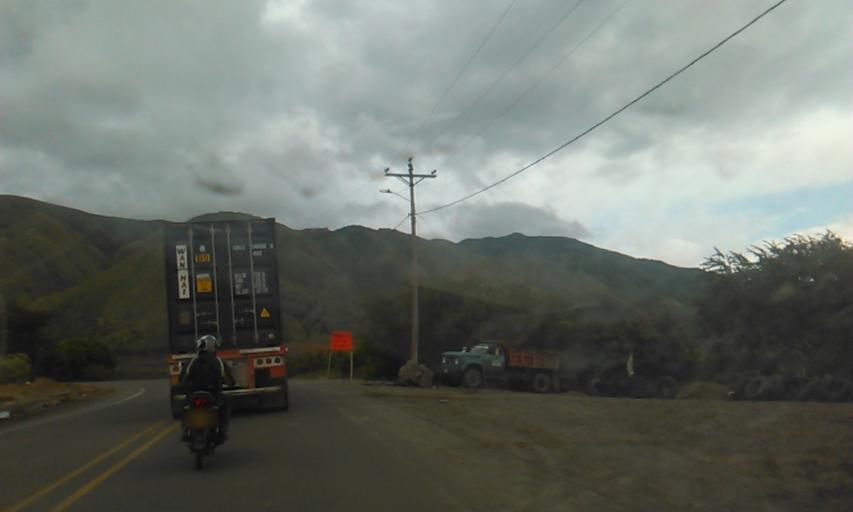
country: CO
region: Valle del Cauca
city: Dagua
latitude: 3.7610
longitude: -76.6636
